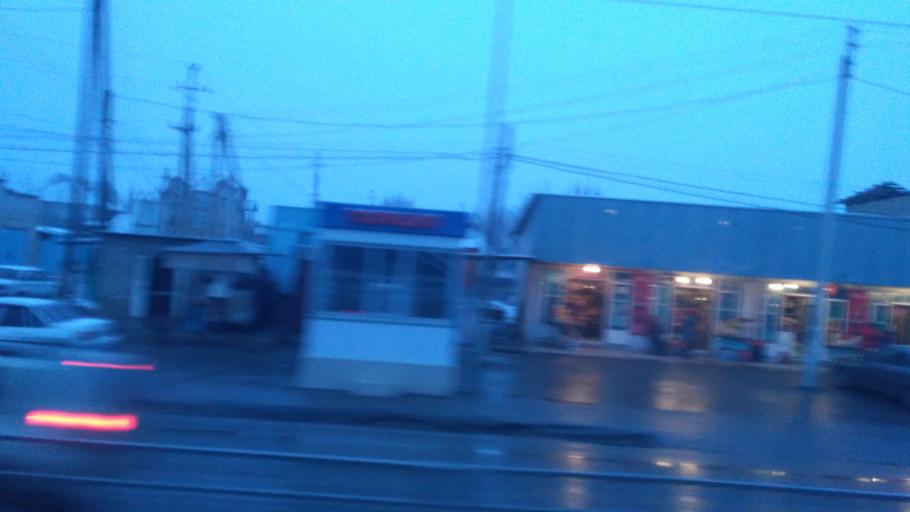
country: KZ
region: Ongtustik Qazaqstan
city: Shymkent
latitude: 42.3736
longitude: 69.5027
